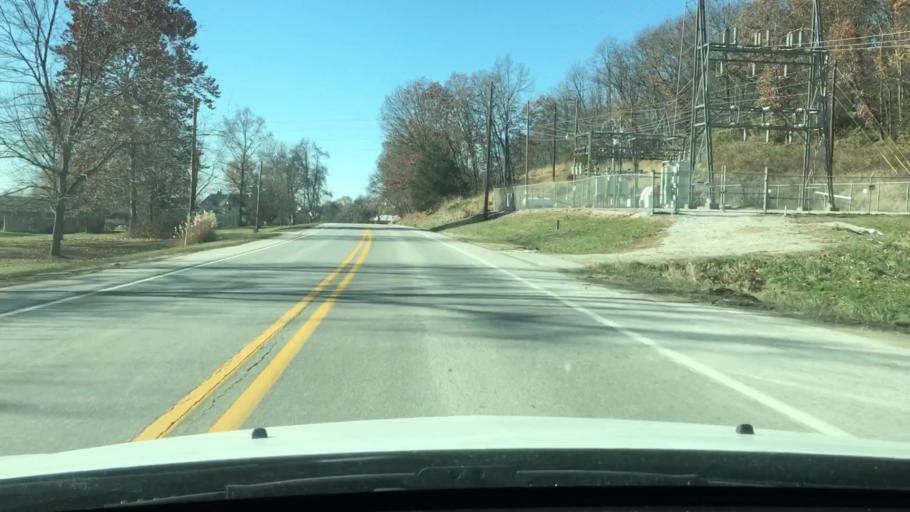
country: US
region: Missouri
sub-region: Pike County
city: Louisiana
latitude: 39.5149
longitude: -90.9649
